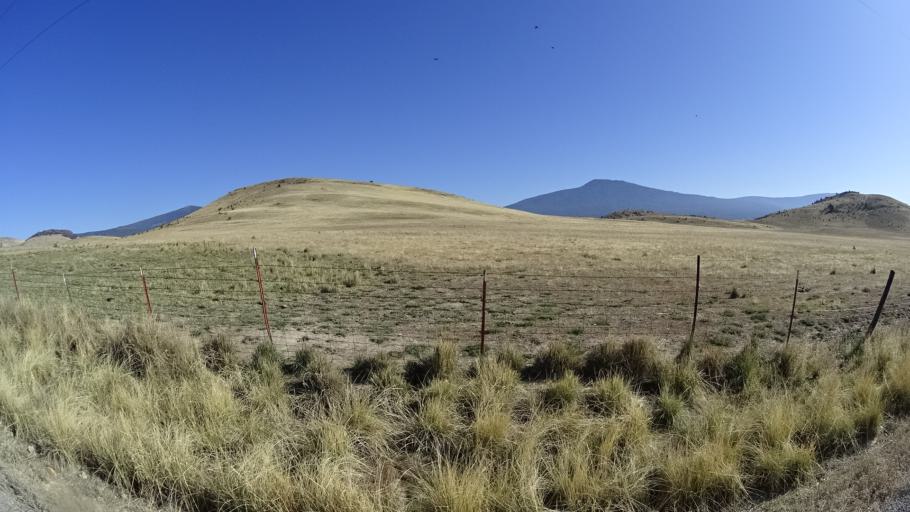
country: US
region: California
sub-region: Siskiyou County
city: Montague
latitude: 41.7564
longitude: -122.3592
